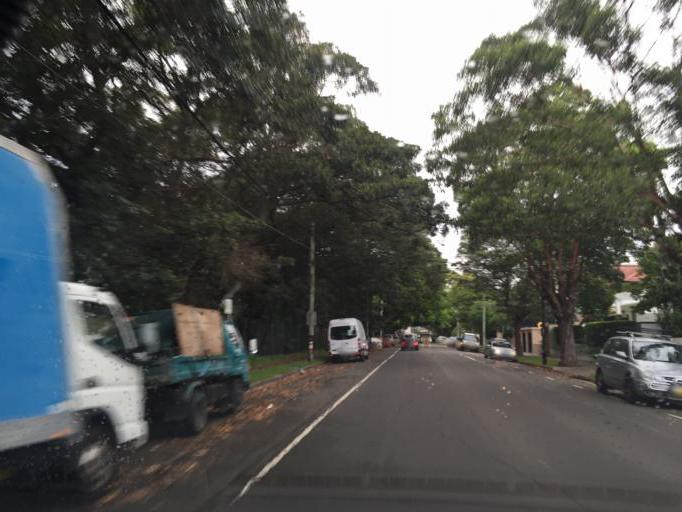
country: AU
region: New South Wales
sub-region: Waverley
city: Bondi Beach
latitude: -33.8830
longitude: 151.2651
